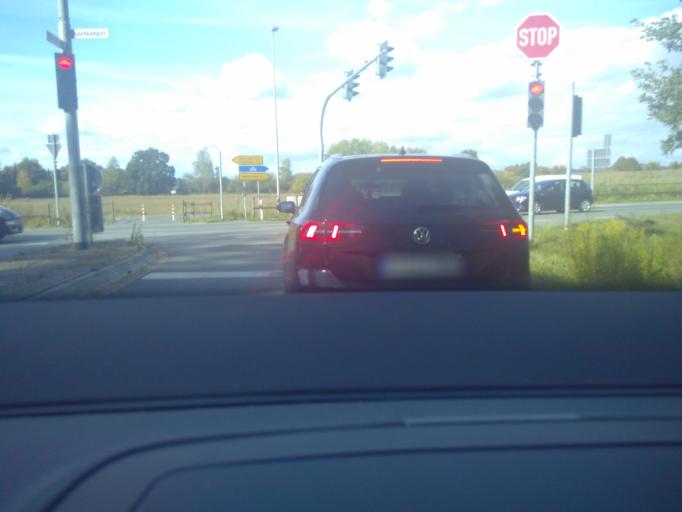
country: DE
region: North Rhine-Westphalia
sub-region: Regierungsbezirk Detmold
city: Verl
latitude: 51.9423
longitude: 8.5156
